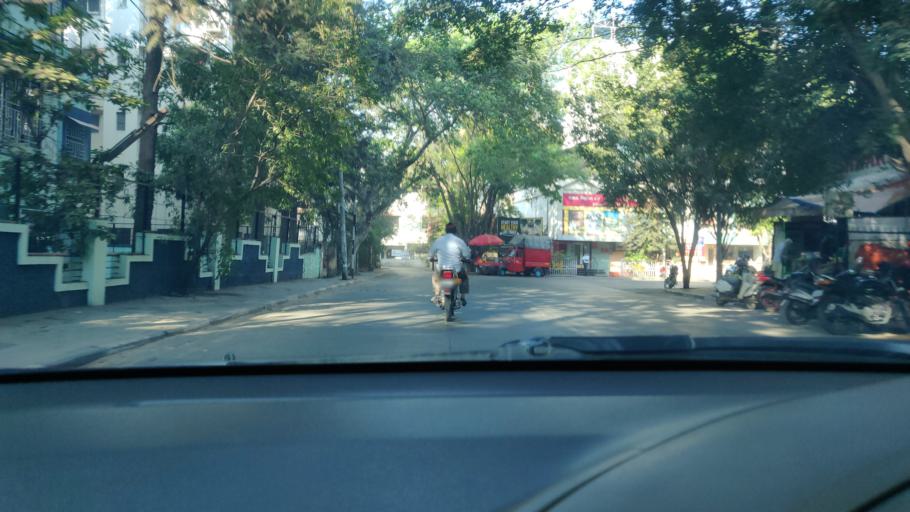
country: IN
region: Maharashtra
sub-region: Pune Division
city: Khadki
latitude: 18.5538
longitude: 73.8053
